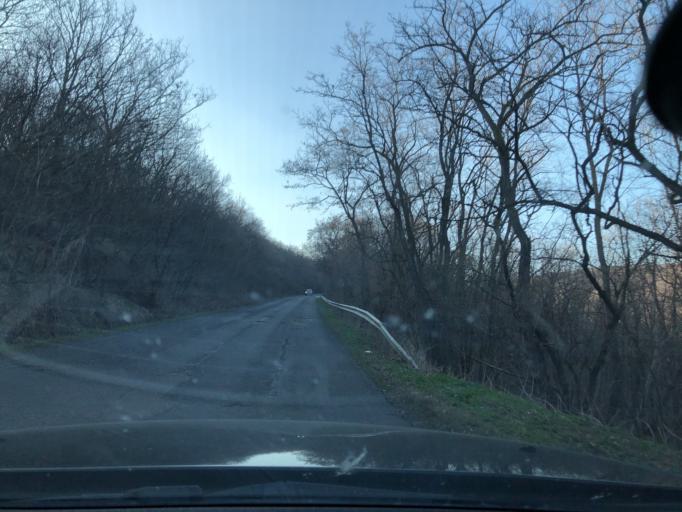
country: HU
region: Nograd
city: Paszto
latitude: 47.9151
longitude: 19.6403
